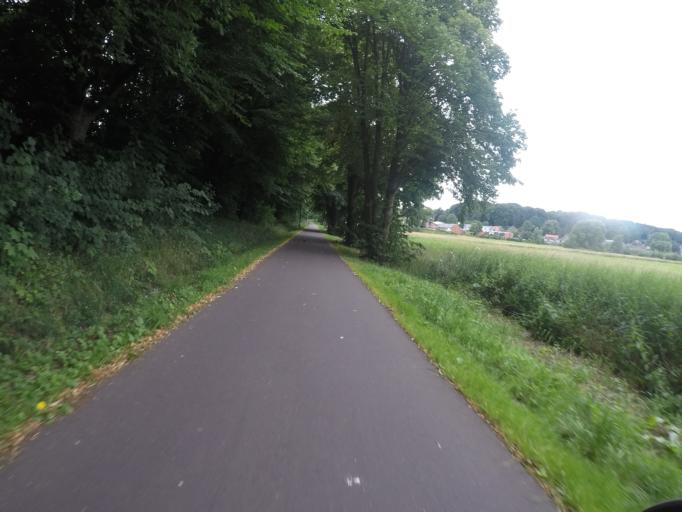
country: DE
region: Lower Saxony
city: Stade
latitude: 53.5981
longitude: 9.4595
